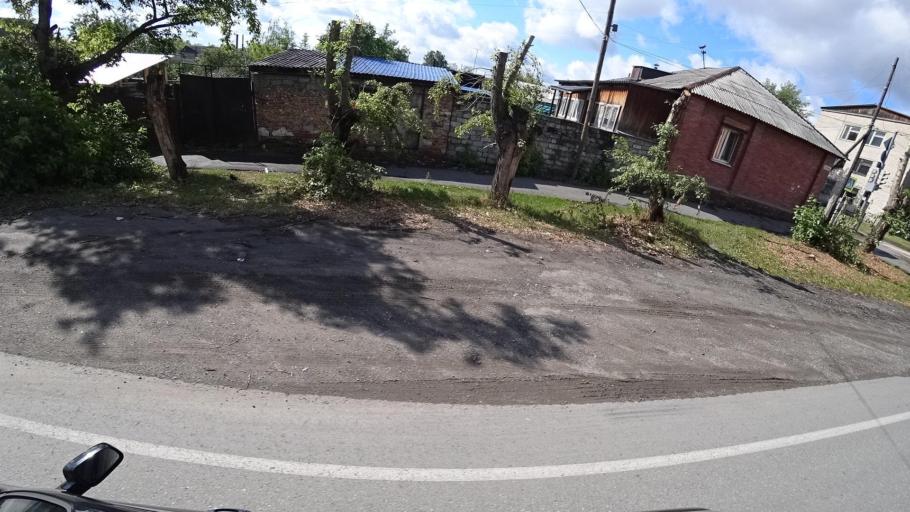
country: RU
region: Sverdlovsk
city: Kamyshlov
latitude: 56.8426
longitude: 62.7064
